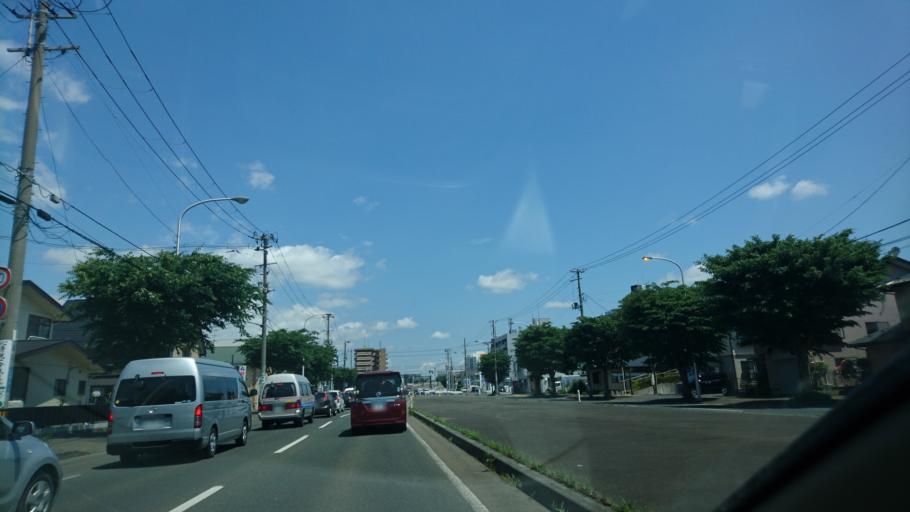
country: JP
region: Iwate
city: Morioka-shi
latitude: 39.6873
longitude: 141.1356
